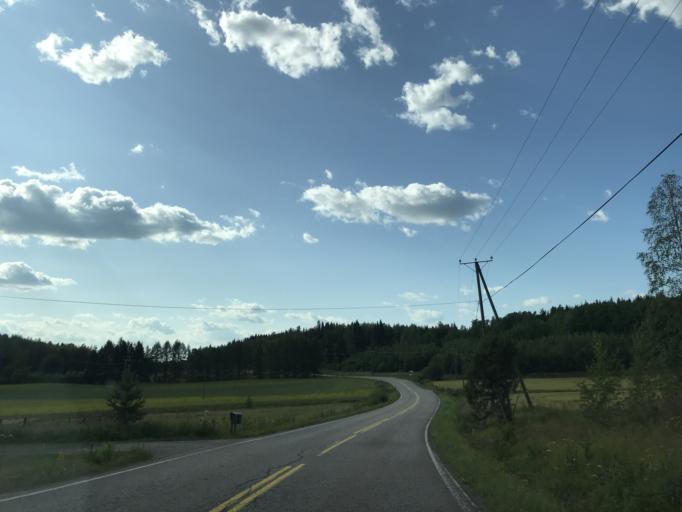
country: FI
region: Uusimaa
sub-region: Helsinki
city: Nurmijaervi
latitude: 60.4502
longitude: 24.6426
